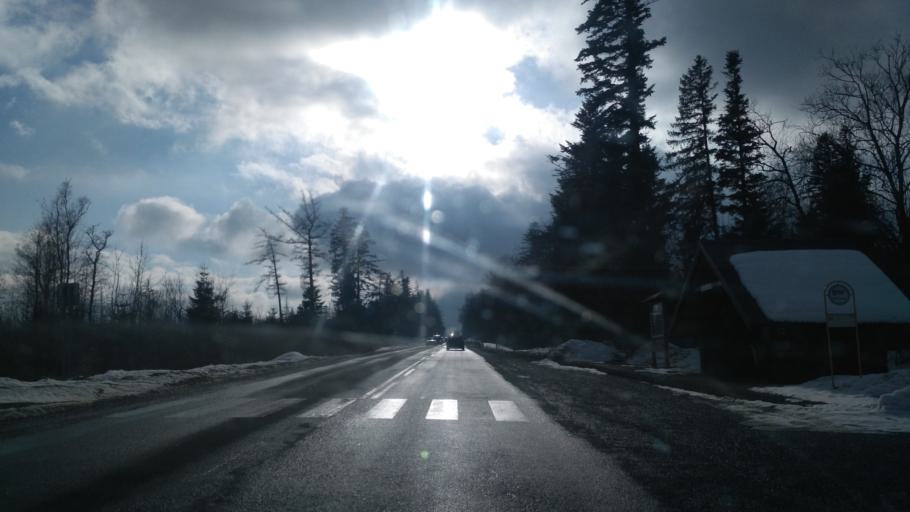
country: SK
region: Presovsky
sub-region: Okres Poprad
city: Nova Lesna
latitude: 49.1943
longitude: 20.3009
